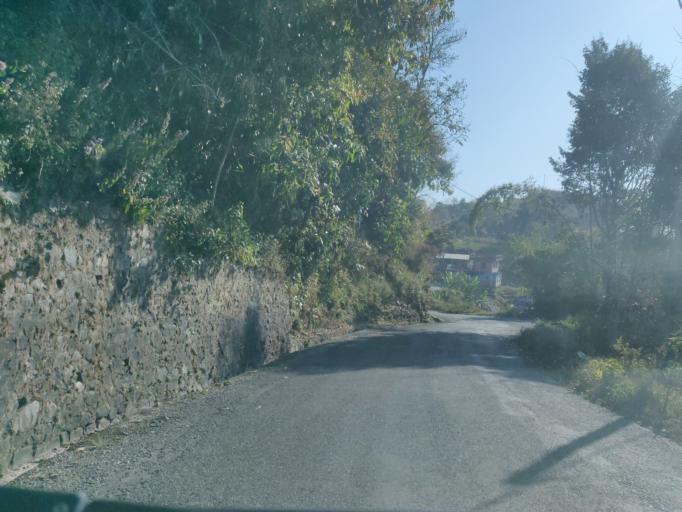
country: NP
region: Western Region
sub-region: Gandaki Zone
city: Pokhara
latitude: 28.2439
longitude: 83.9584
